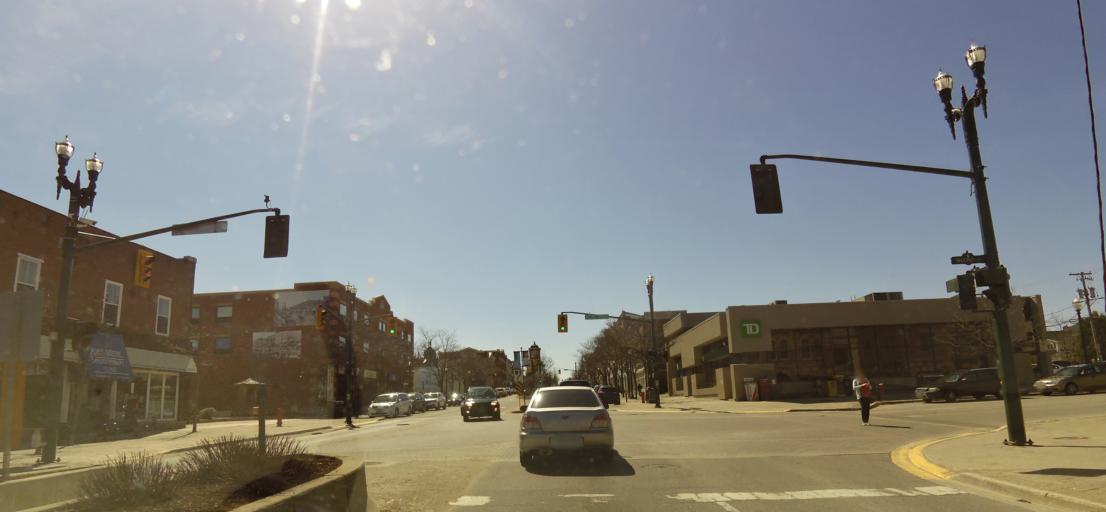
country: CA
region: Ontario
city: Orangeville
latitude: 43.9200
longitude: -80.0941
